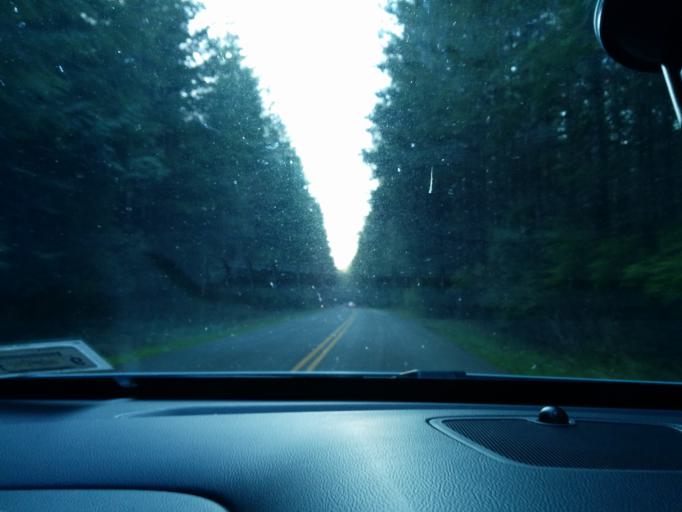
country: US
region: Washington
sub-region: Snohomish County
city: Gold Bar
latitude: 47.8932
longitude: -121.7401
